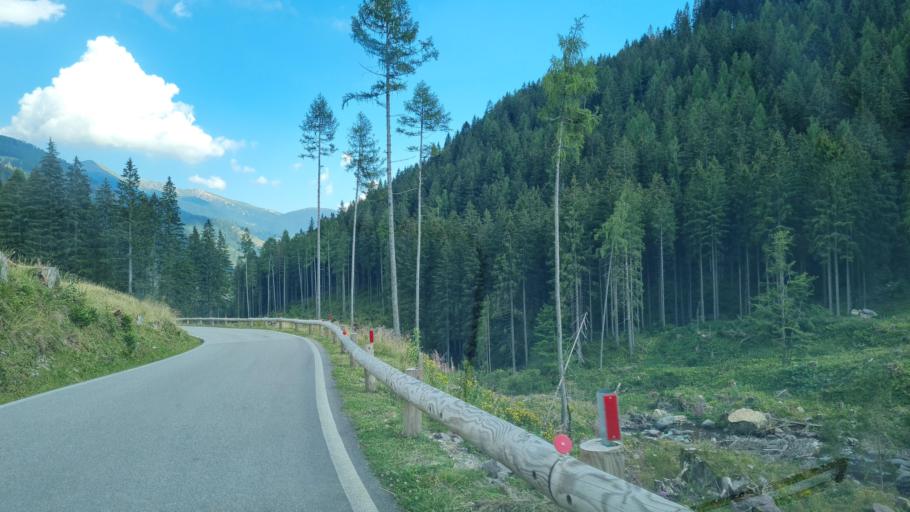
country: IT
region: Trentino-Alto Adige
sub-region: Provincia di Trento
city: Torcegno
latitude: 46.1498
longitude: 11.4508
